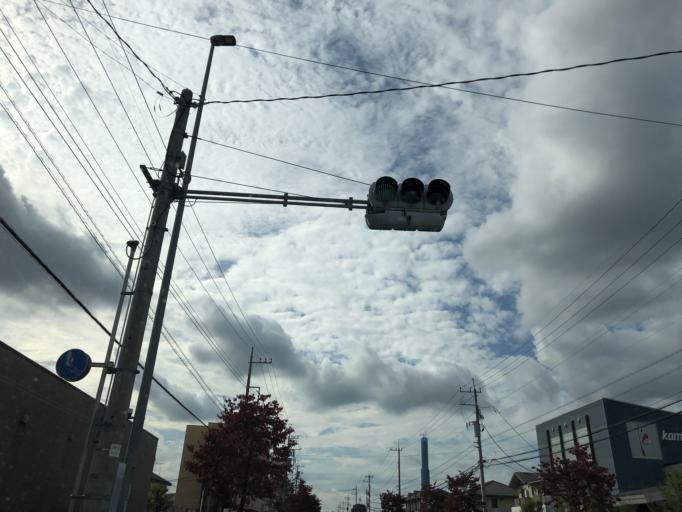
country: JP
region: Tochigi
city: Sano
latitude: 36.2994
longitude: 139.6023
